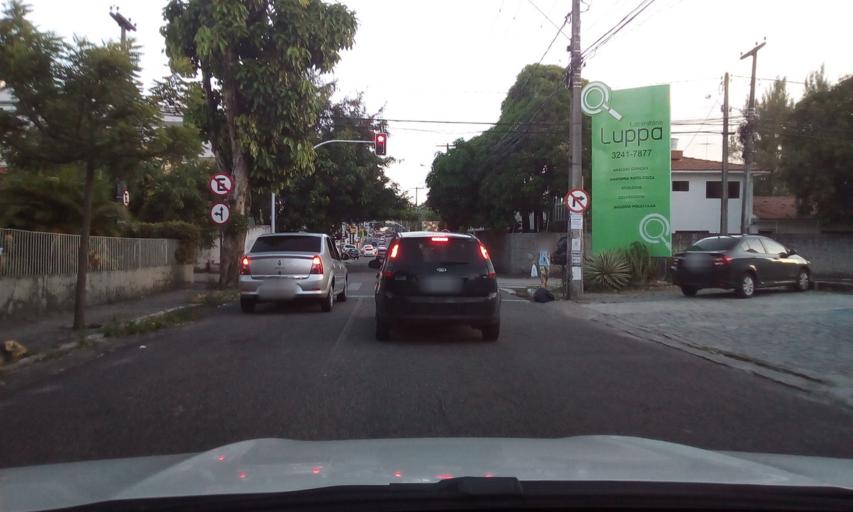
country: BR
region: Paraiba
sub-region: Joao Pessoa
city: Joao Pessoa
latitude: -7.1173
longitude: -34.8553
